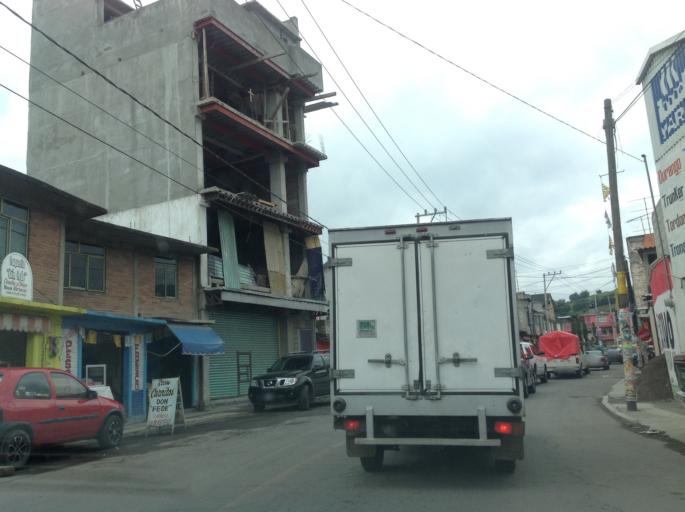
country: MX
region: Mexico
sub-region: Tenango del Valle
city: Santa Maria Jajalpa
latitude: 19.1130
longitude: -99.5370
